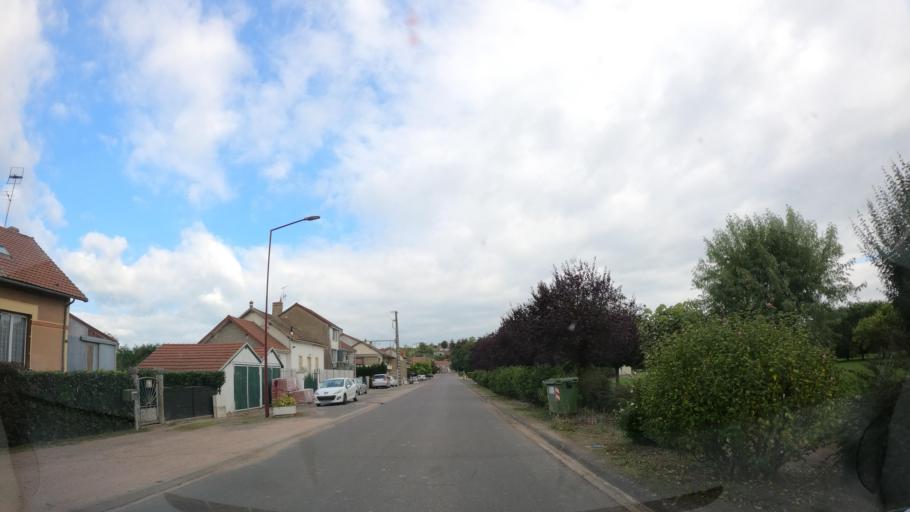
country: FR
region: Auvergne
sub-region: Departement de l'Allier
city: Lapalisse
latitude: 46.3274
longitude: 3.5897
